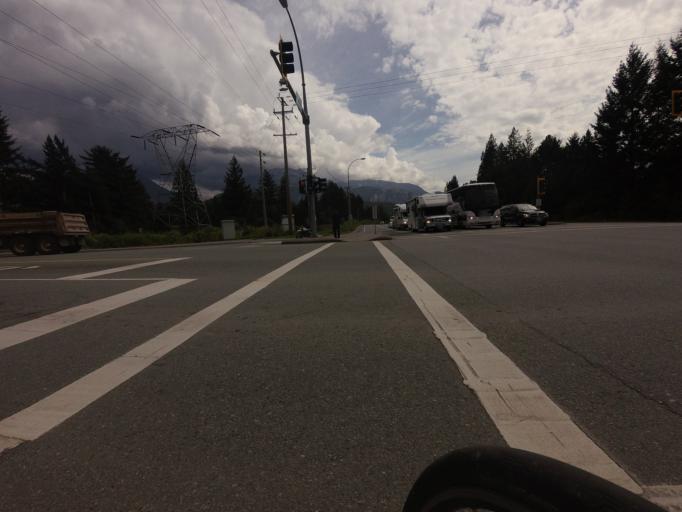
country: CA
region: British Columbia
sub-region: Greater Vancouver Regional District
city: Lions Bay
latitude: 49.7350
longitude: -123.1347
